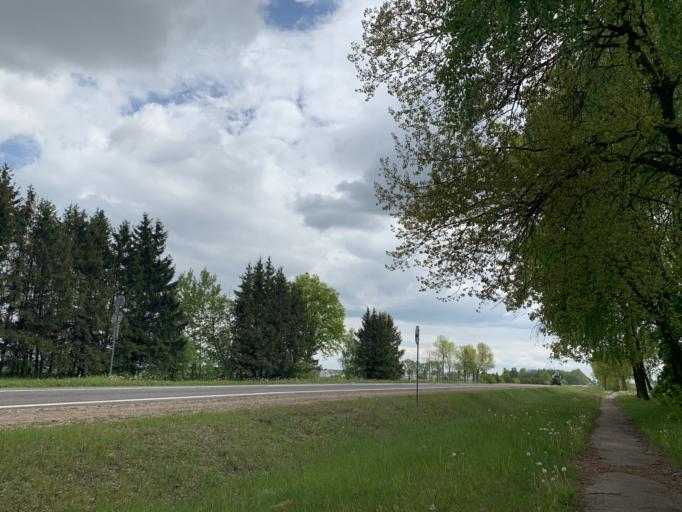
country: BY
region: Minsk
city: Nyasvizh
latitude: 53.2440
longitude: 26.6763
